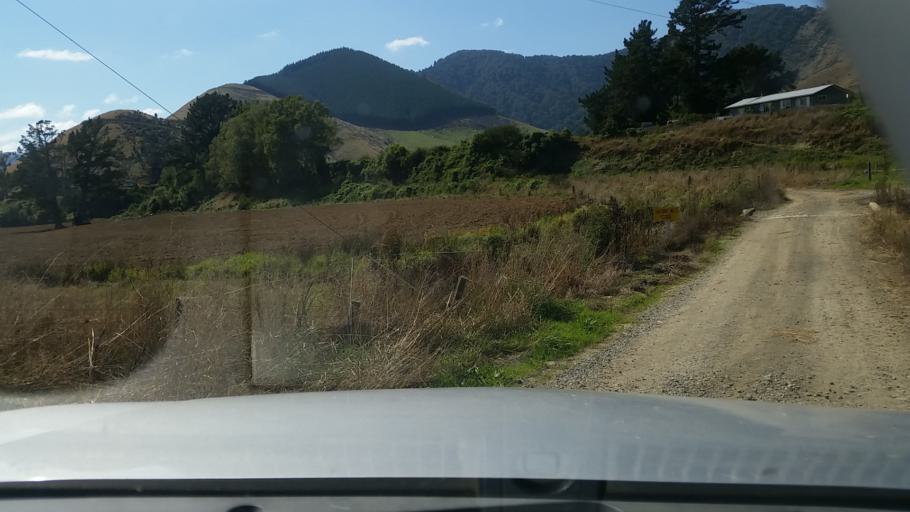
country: NZ
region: Nelson
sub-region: Nelson City
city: Nelson
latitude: -41.2503
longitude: 173.5832
